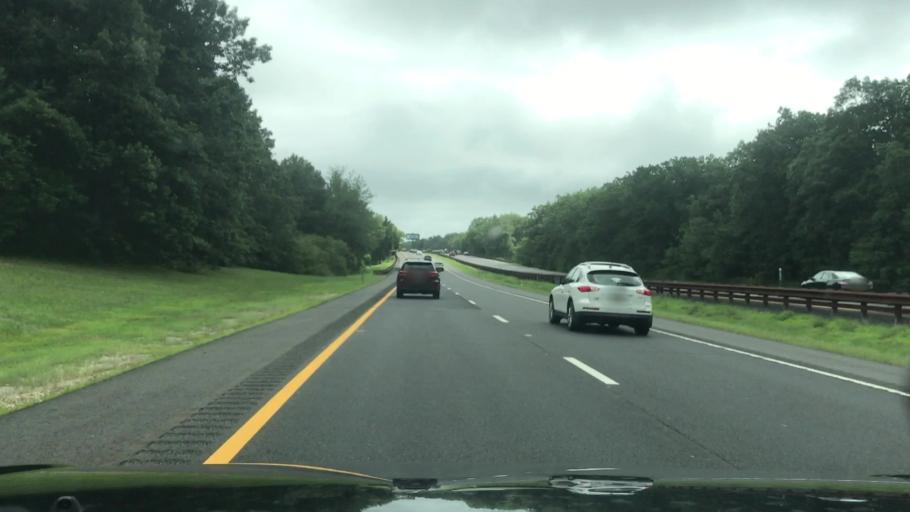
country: US
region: New Jersey
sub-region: Monmouth County
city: Eatontown
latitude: 40.2630
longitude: -74.0799
